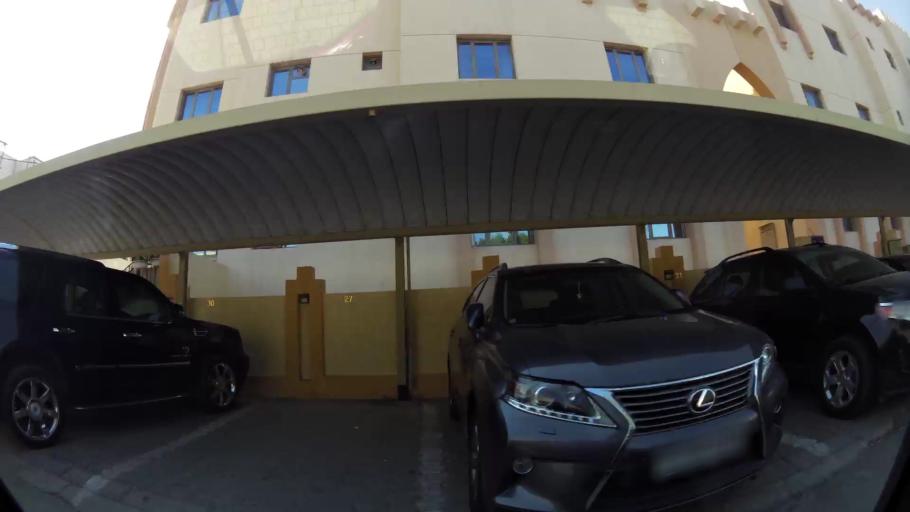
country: KW
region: Muhafazat Hawalli
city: Salwa
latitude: 29.2842
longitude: 48.0811
